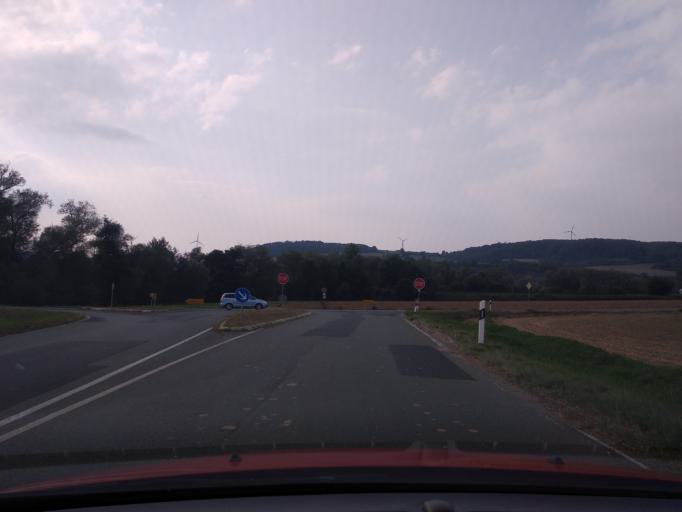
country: DE
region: Hesse
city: Liebenau
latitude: 51.4967
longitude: 9.2959
